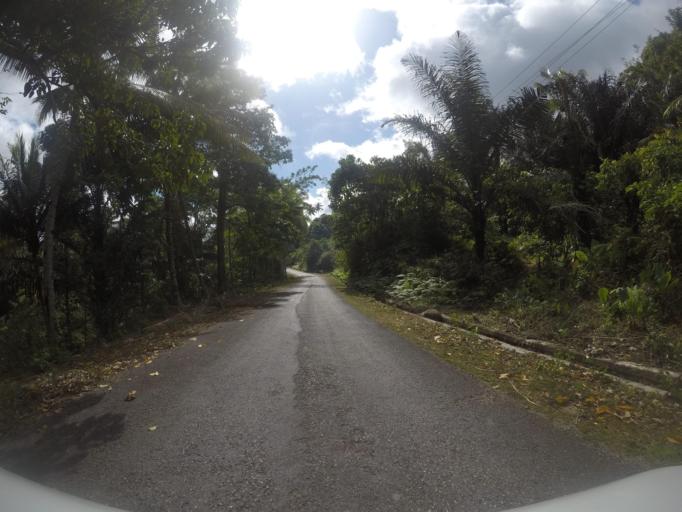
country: TL
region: Lautem
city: Lospalos
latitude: -8.5340
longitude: 126.9318
